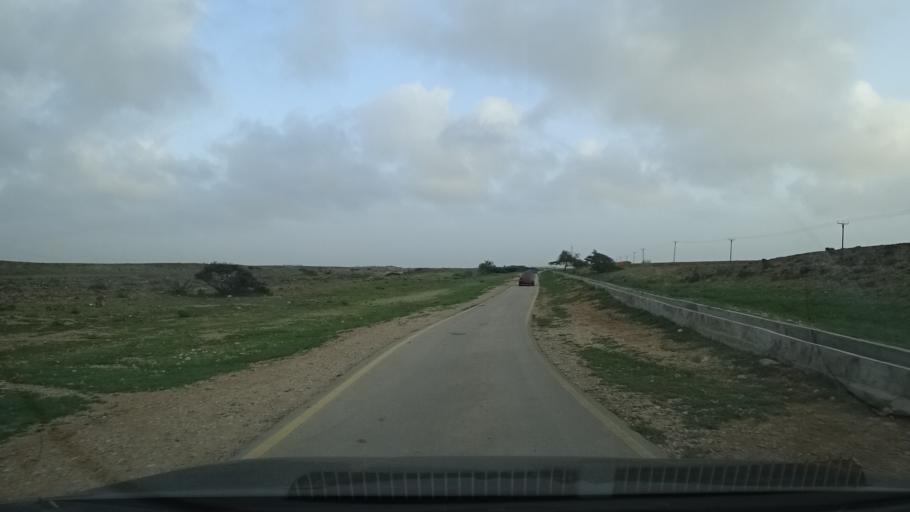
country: OM
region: Zufar
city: Salalah
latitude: 17.0954
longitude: 54.2333
